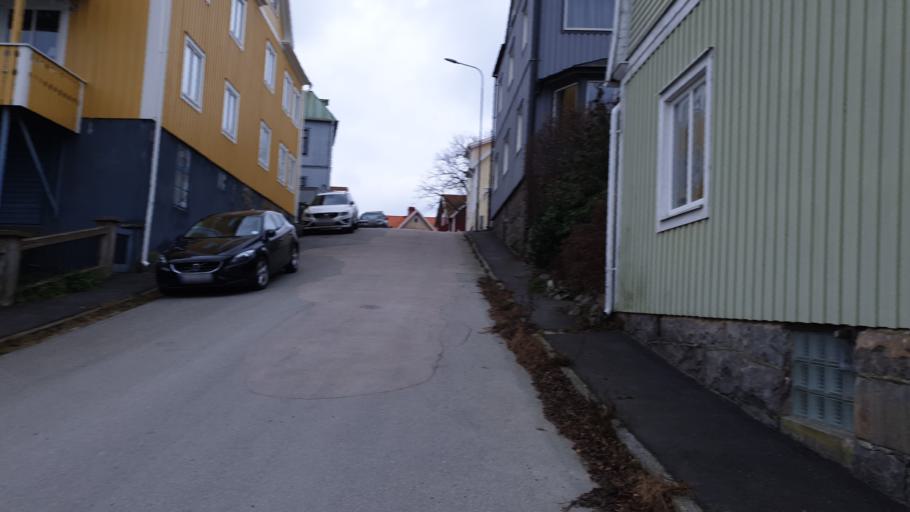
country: SE
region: Blekinge
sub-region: Karlskrona Kommun
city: Karlskrona
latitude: 56.1656
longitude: 15.5724
